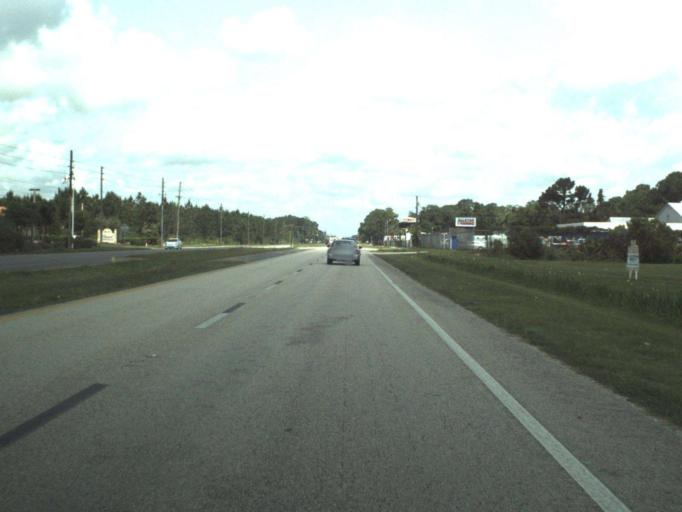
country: US
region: Florida
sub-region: Volusia County
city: Ormond-by-the-Sea
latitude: 29.3255
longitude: -81.1167
